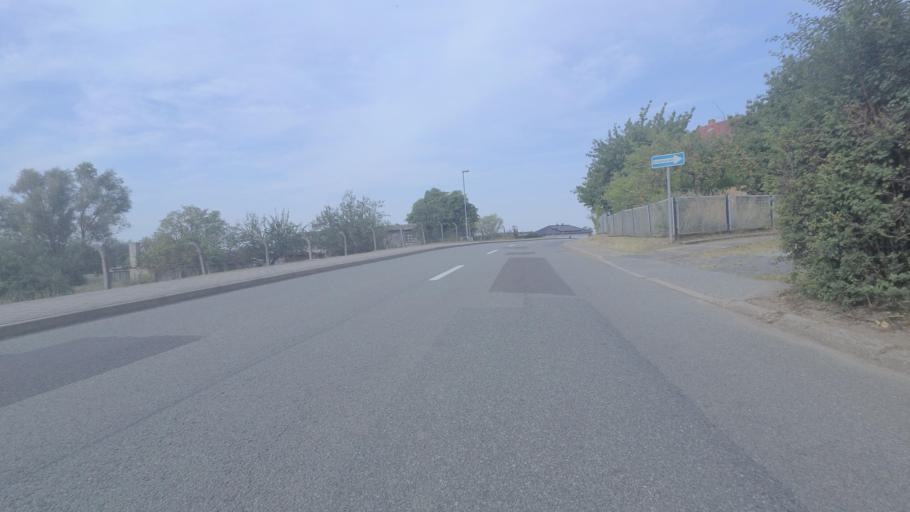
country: DE
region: Mecklenburg-Vorpommern
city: Gielow
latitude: 53.6475
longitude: 12.8324
